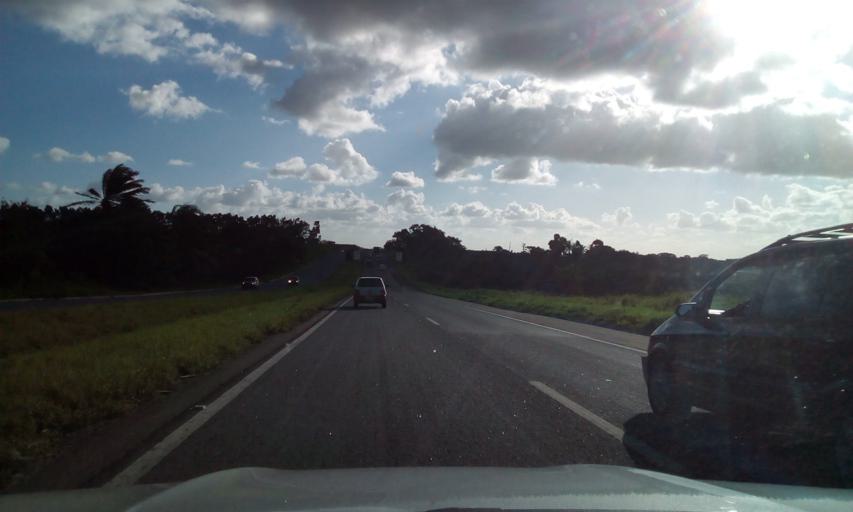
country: BR
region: Paraiba
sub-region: Cruz Do Espirito Santo
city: Cruz do Espirito Santo
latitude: -7.2035
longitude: -35.1213
